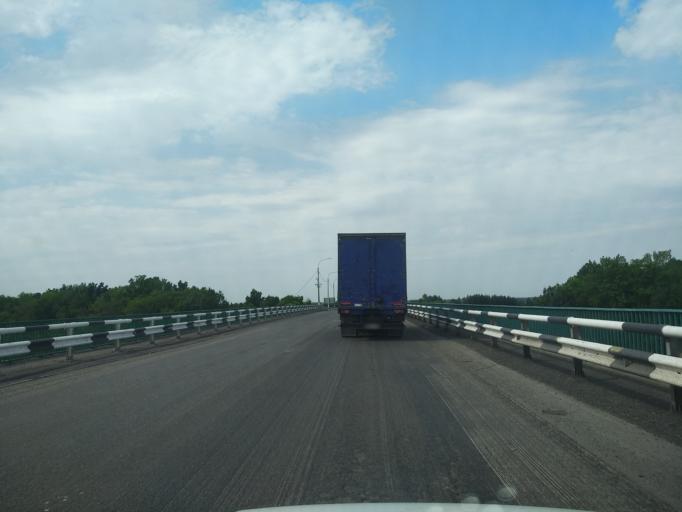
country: RU
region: Voronezj
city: Pereleshino
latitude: 51.7622
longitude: 40.1272
